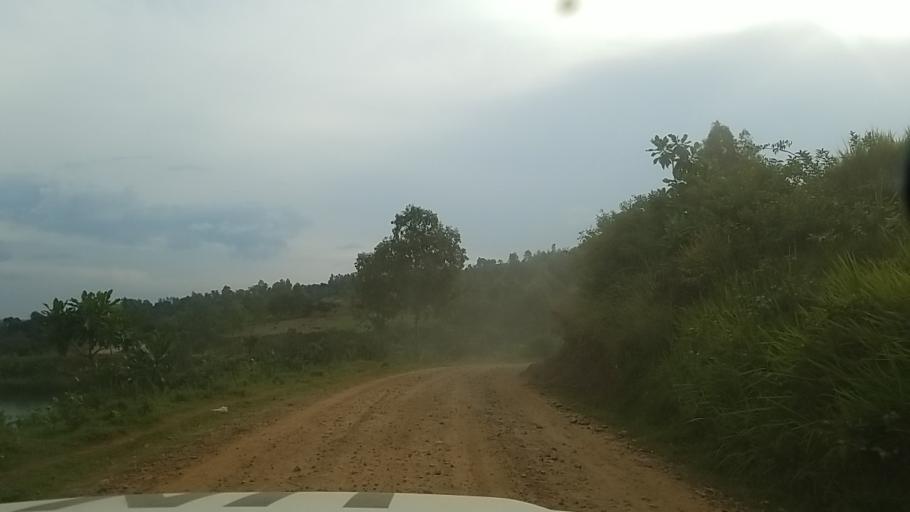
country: RW
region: Western Province
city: Cyangugu
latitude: -2.1066
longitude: 28.9072
